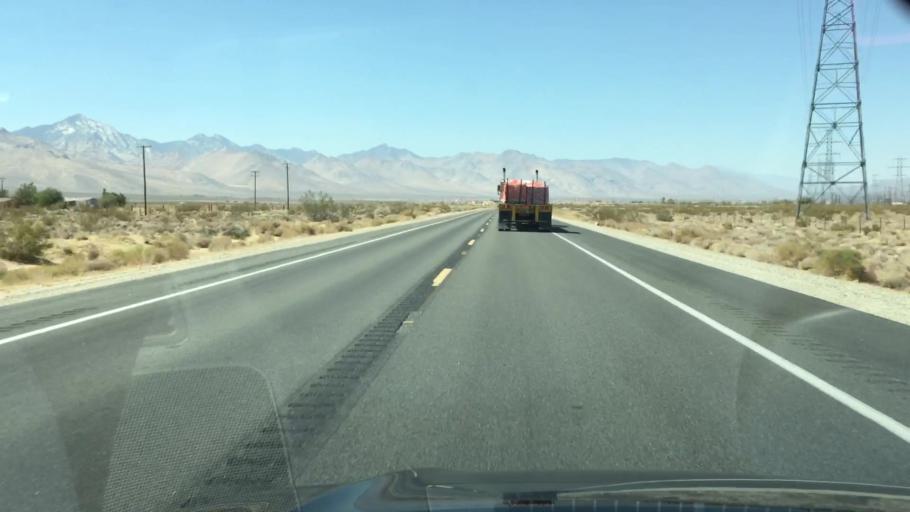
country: US
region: California
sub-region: Kern County
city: Inyokern
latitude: 35.6421
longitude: -117.7926
